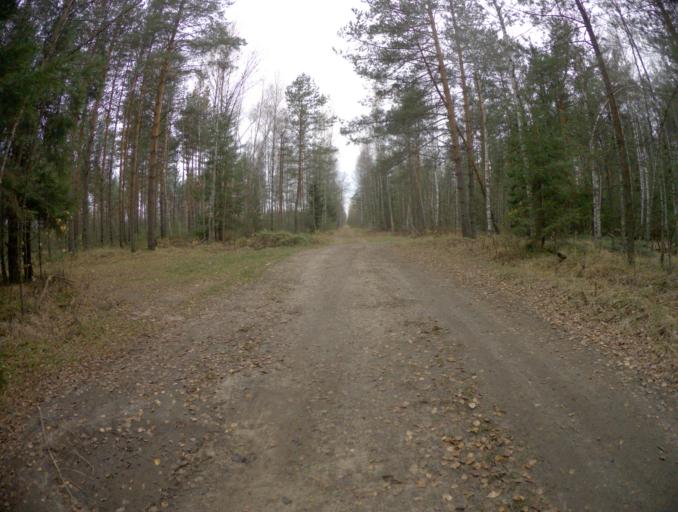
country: RU
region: Moskovskaya
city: Malaya Dubna
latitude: 55.9416
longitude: 38.9683
